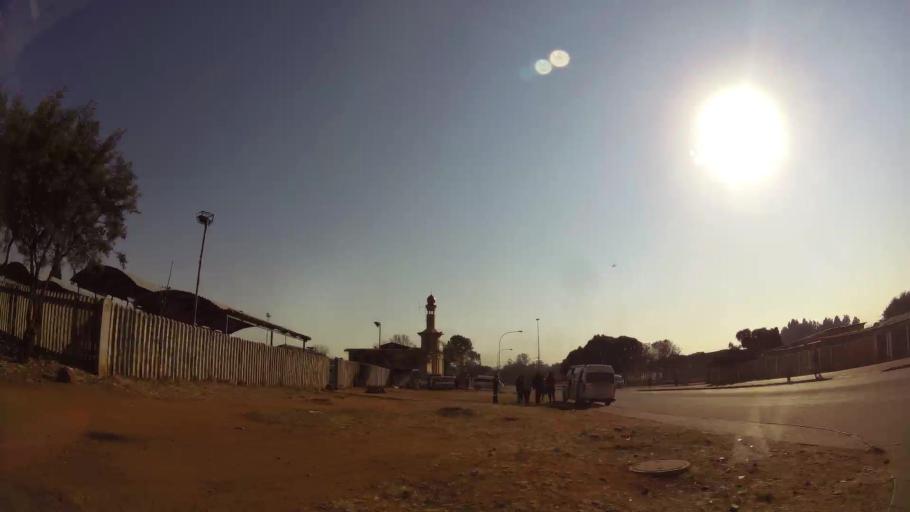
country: ZA
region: Gauteng
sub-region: Ekurhuleni Metropolitan Municipality
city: Boksburg
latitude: -26.2301
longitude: 28.2264
